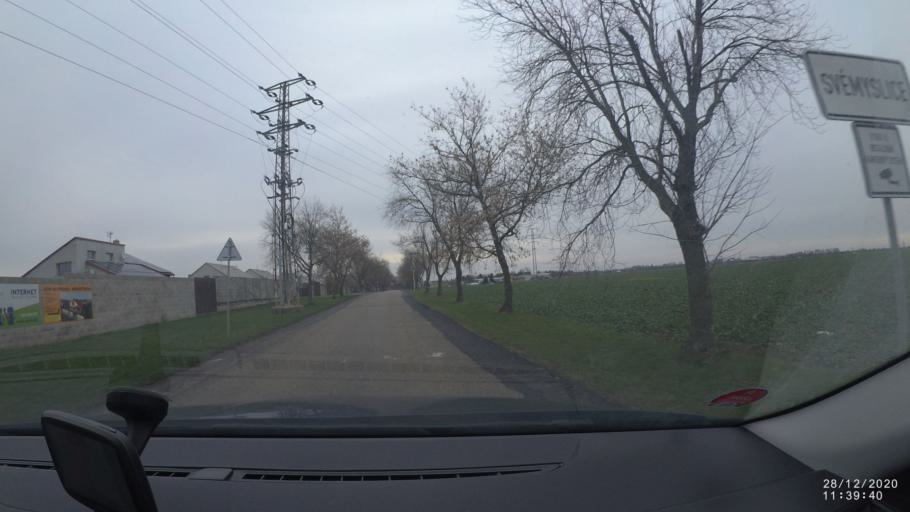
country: CZ
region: Central Bohemia
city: Zelenec
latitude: 50.1447
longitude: 14.6410
